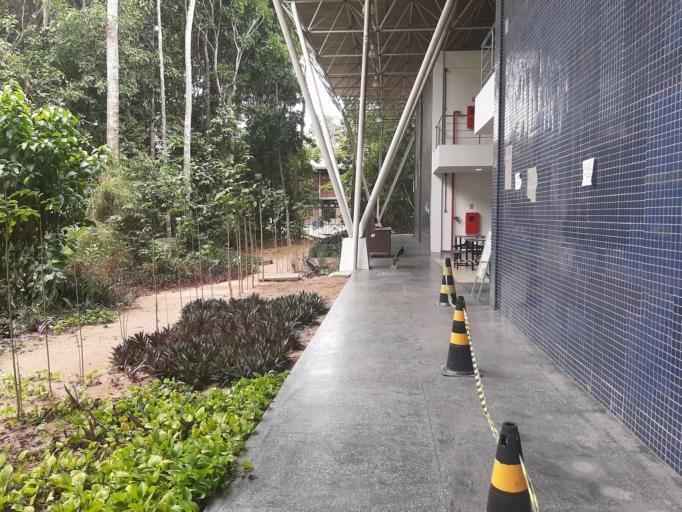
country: BR
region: Amazonas
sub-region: Manaus
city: Manaus
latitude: -3.0899
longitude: -59.9642
